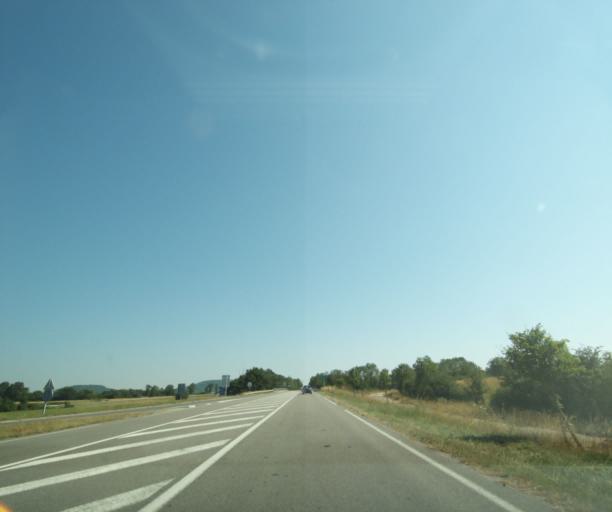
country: FR
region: Lorraine
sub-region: Departement de Meurthe-et-Moselle
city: Ecrouves
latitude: 48.6485
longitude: 5.8694
